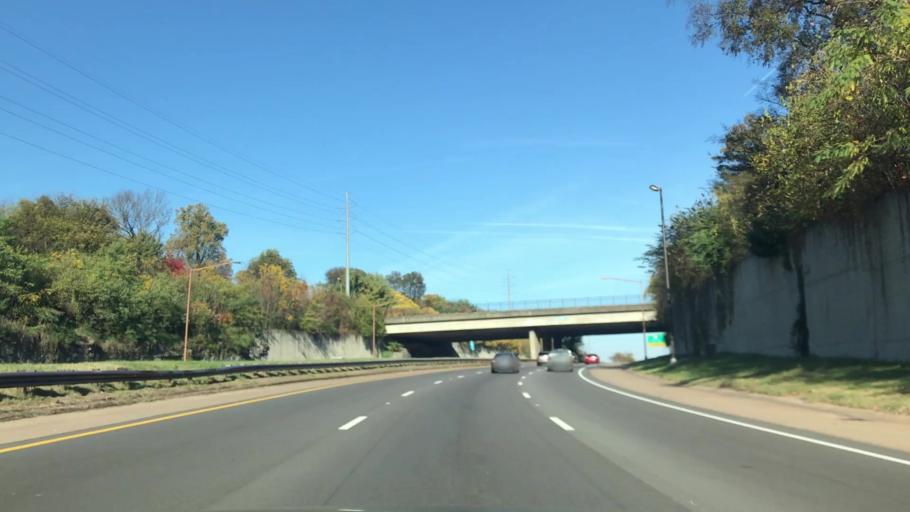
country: US
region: Tennessee
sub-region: Davidson County
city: Oak Hill
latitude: 36.1134
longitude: -86.7981
